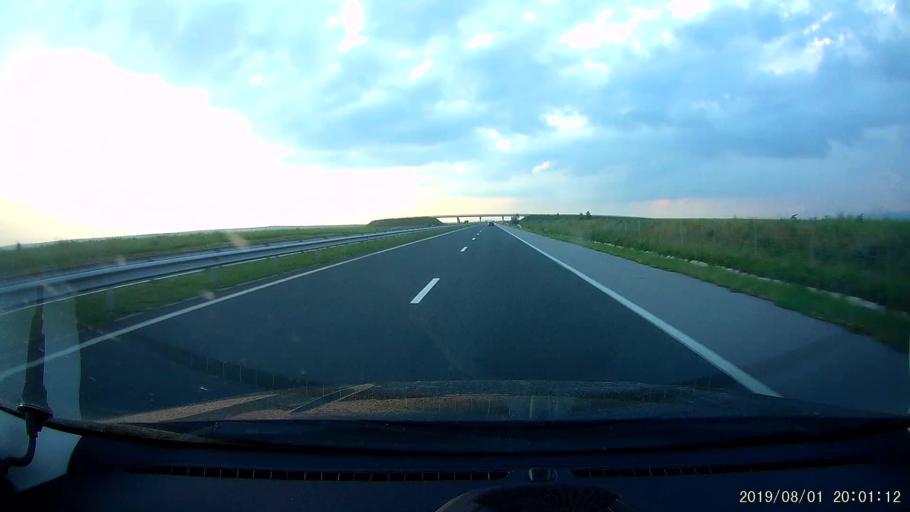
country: BG
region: Yambol
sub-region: Obshtina Straldzha
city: Straldzha
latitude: 42.5563
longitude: 26.6740
